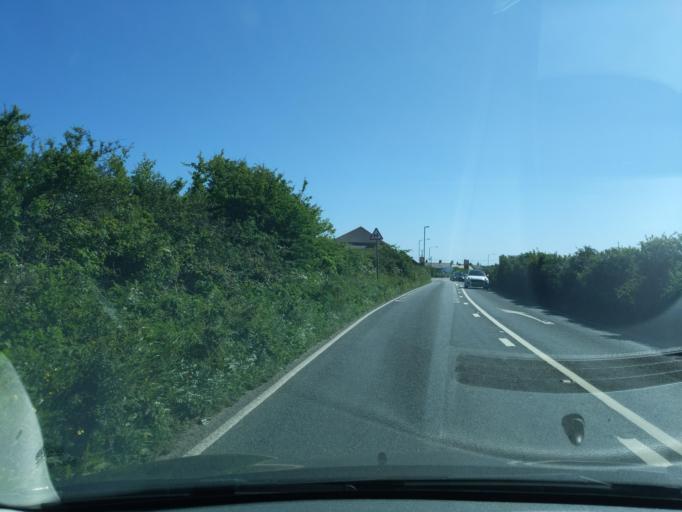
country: GB
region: England
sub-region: Cornwall
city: Wendron
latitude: 50.1151
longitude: -5.2450
